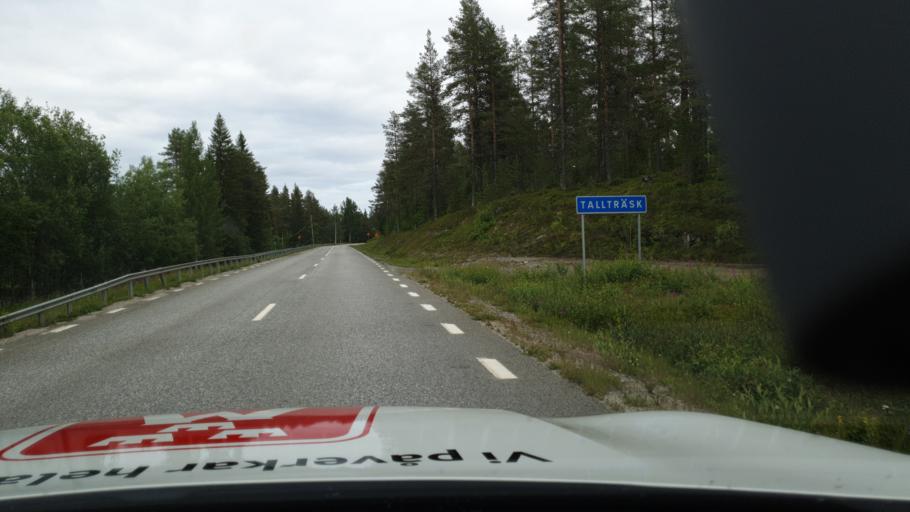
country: SE
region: Vaesterbotten
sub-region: Lycksele Kommun
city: Soderfors
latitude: 64.6153
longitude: 18.1788
